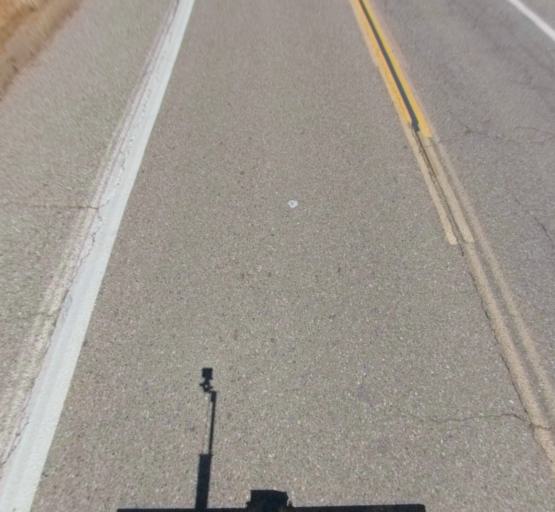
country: US
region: California
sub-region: Madera County
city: Fairmead
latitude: 37.0404
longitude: -120.1622
